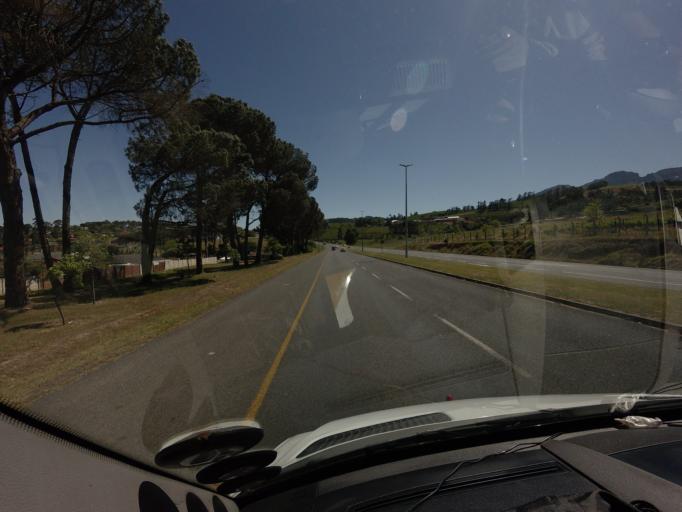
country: ZA
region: Western Cape
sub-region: Cape Winelands District Municipality
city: Stellenbosch
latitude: -33.9128
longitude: 18.8590
